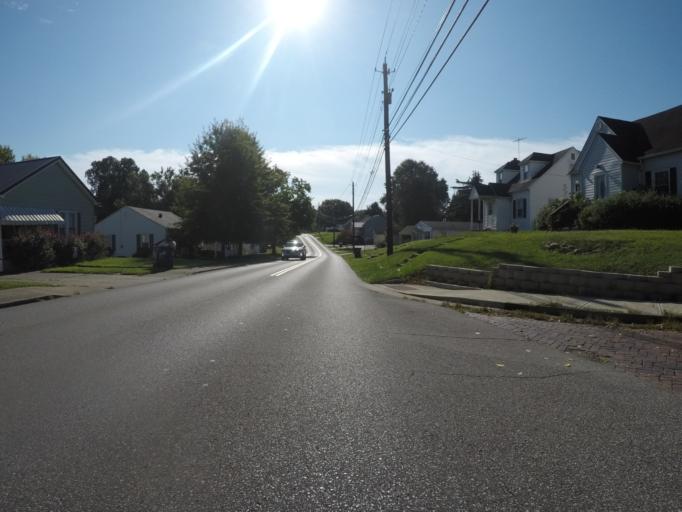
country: US
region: Kentucky
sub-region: Boyd County
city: Ashland
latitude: 38.4515
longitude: -82.6328
